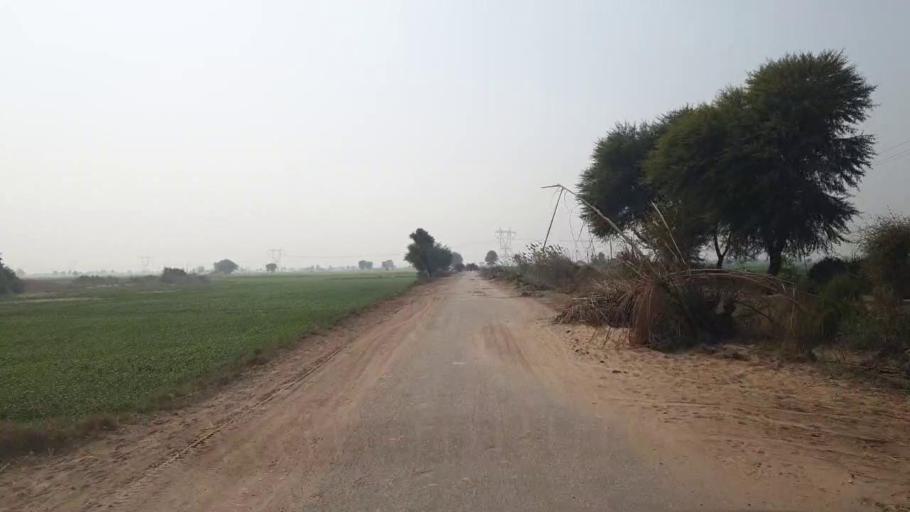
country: PK
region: Sindh
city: Hala
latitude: 25.9447
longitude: 68.4505
